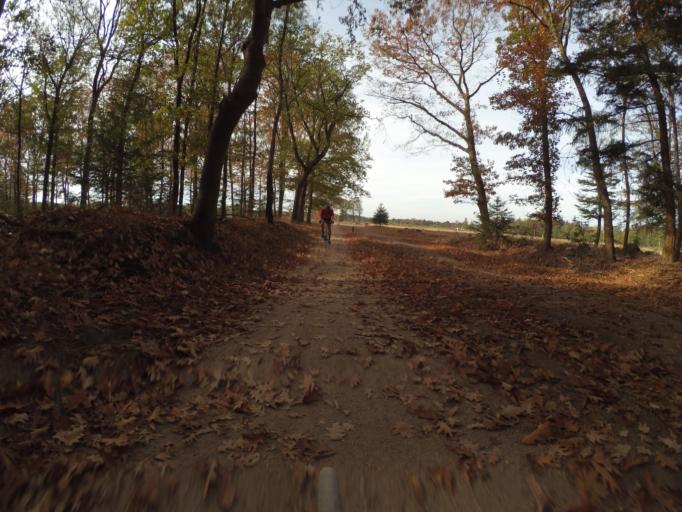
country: NL
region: Overijssel
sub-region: Gemeente Twenterand
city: Den Ham
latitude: 52.3633
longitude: 6.4228
